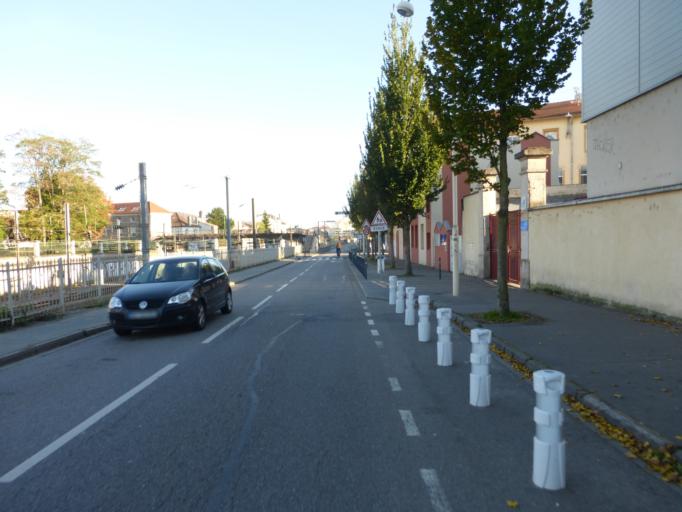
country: FR
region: Lorraine
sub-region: Departement de Meurthe-et-Moselle
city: Nancy
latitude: 48.6822
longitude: 6.1849
